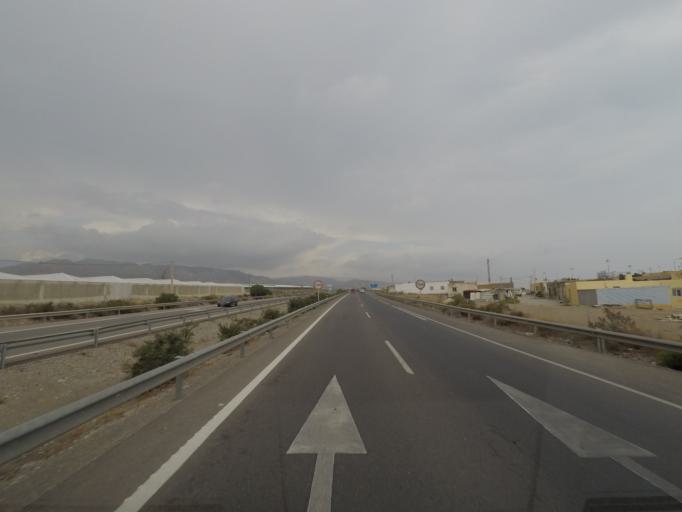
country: ES
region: Andalusia
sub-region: Provincia de Almeria
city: Vicar
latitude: 36.7982
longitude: -2.6821
